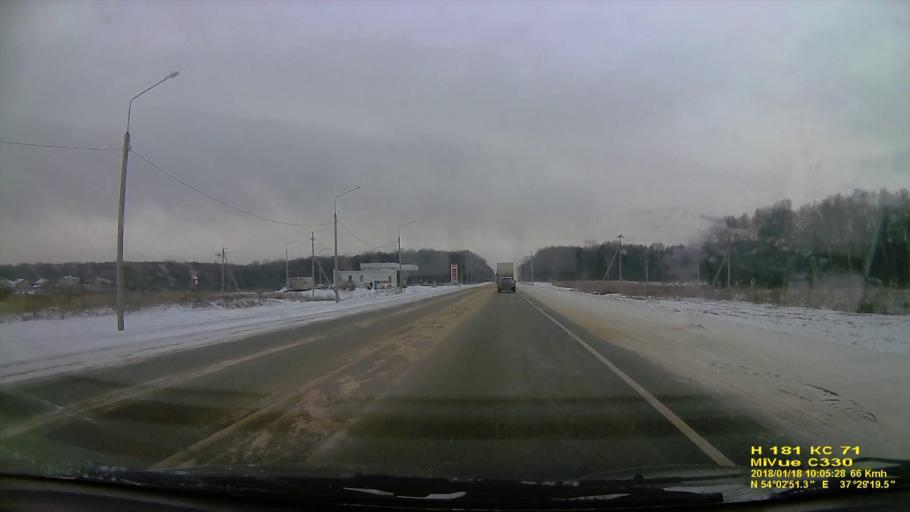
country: RU
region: Tula
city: Pervomayskiy
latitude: 54.0474
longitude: 37.4887
